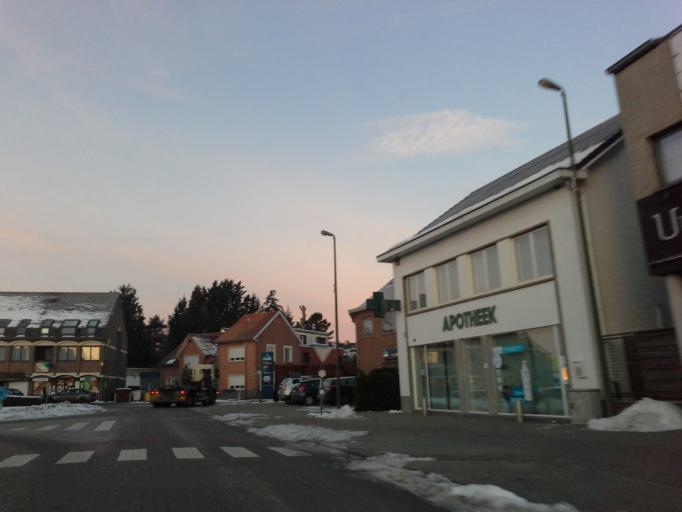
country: BE
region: Flanders
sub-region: Provincie Vlaams-Brabant
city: Lubbeek
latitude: 50.8818
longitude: 4.8418
